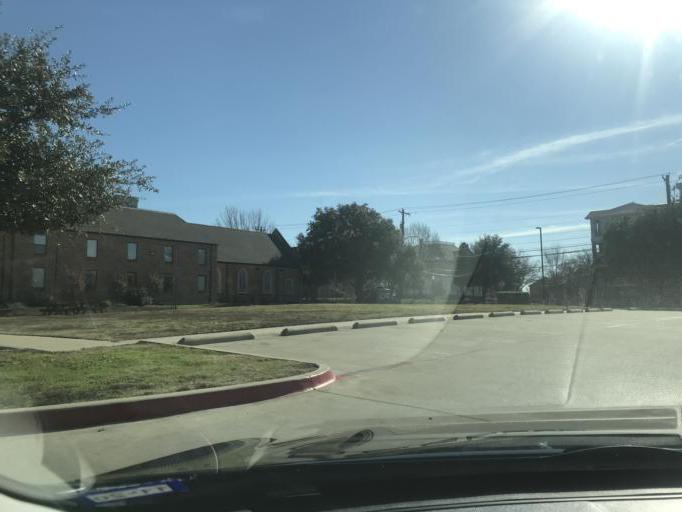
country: US
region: Texas
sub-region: Denton County
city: Denton
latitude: 33.2163
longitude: -97.1447
